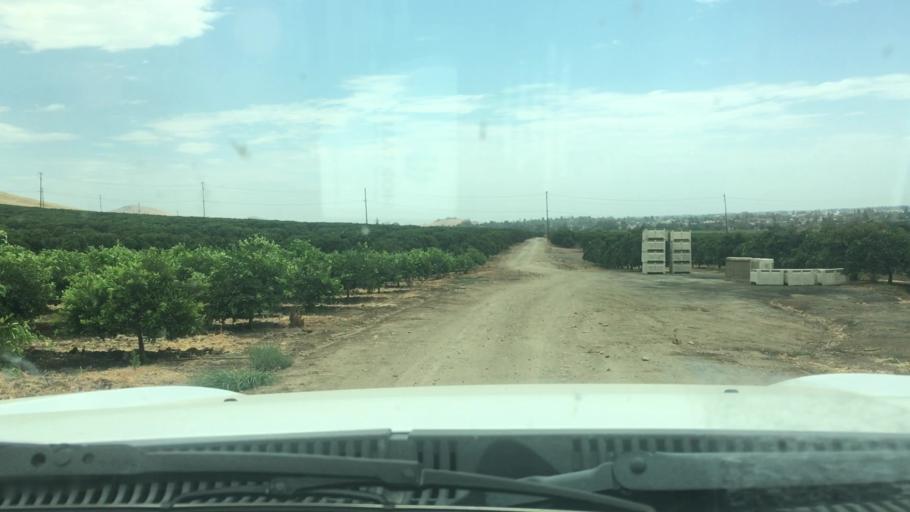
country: US
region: California
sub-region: Tulare County
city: Porterville
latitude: 36.0981
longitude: -119.0045
